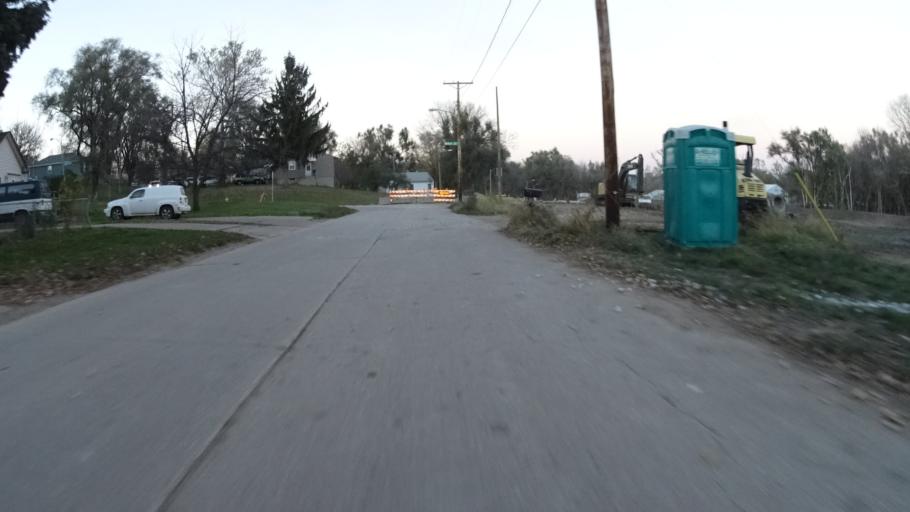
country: US
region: Nebraska
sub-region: Douglas County
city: Omaha
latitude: 41.1904
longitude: -95.9503
